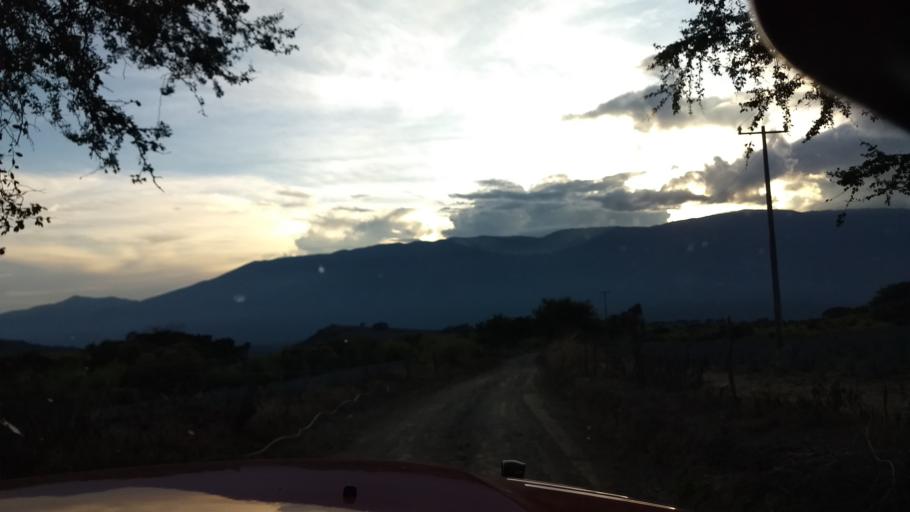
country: MX
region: Colima
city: Suchitlan
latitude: 19.4944
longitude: -103.7803
